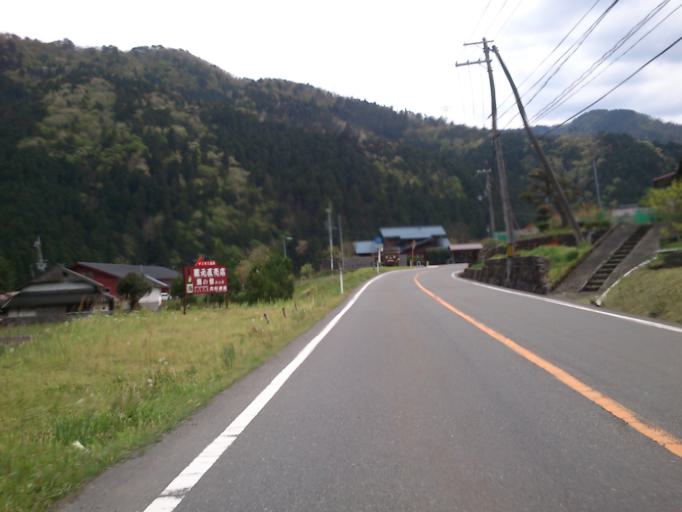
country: JP
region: Fukui
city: Obama
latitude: 35.3045
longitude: 135.6200
